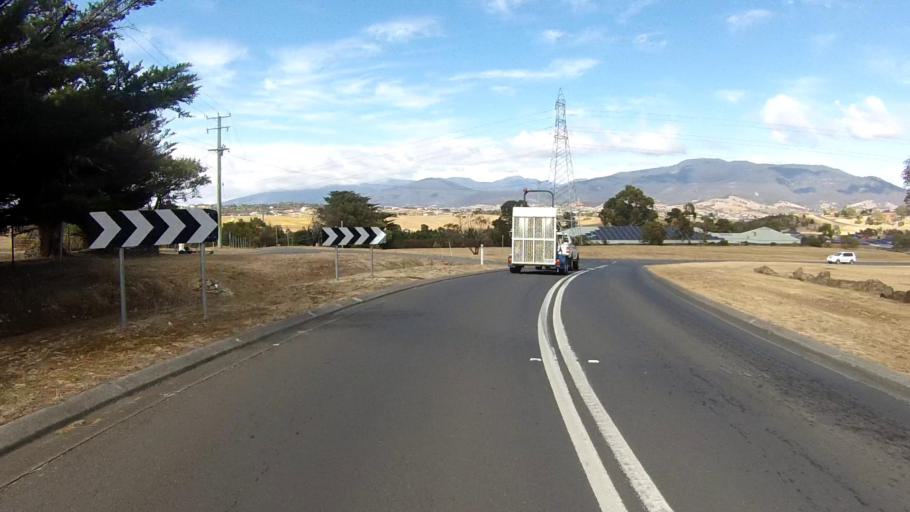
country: AU
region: Tasmania
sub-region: Brighton
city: Old Beach
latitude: -42.7502
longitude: 147.2798
